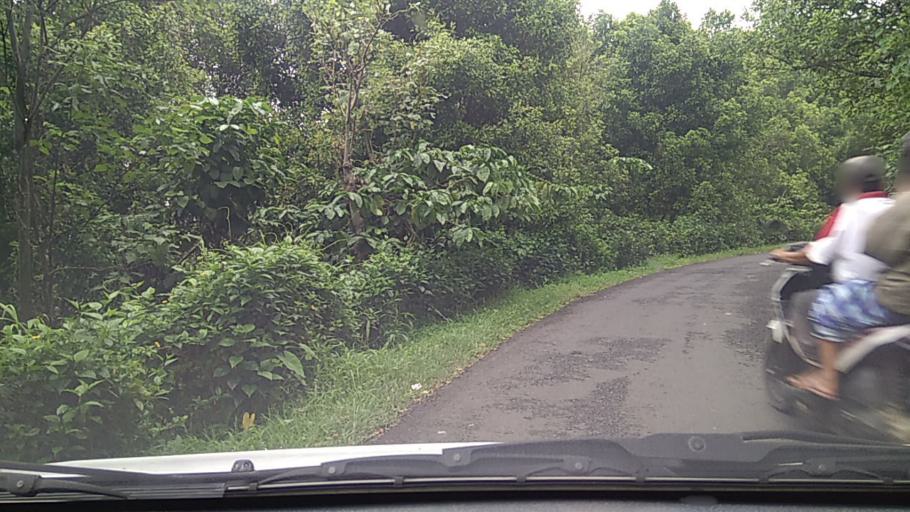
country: ID
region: Bali
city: Banjar Padangbulia
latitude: -8.1782
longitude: 115.1869
